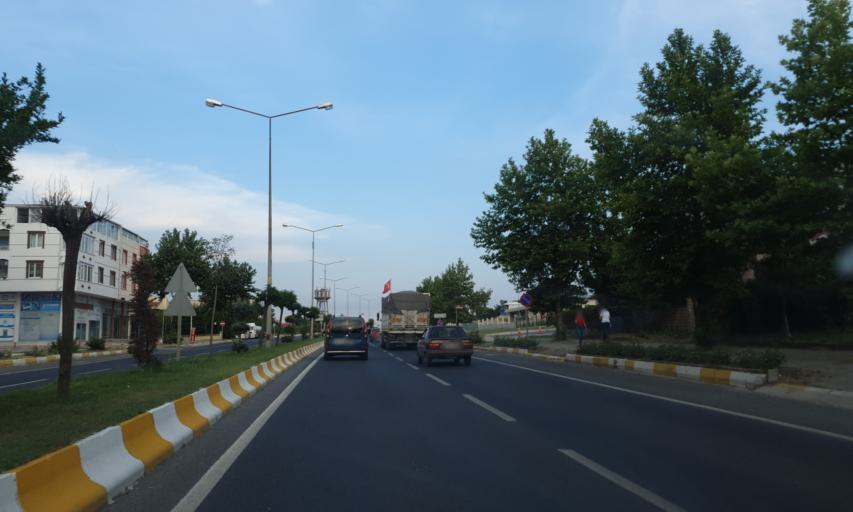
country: TR
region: Kirklareli
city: Luleburgaz
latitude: 41.4004
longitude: 27.3728
